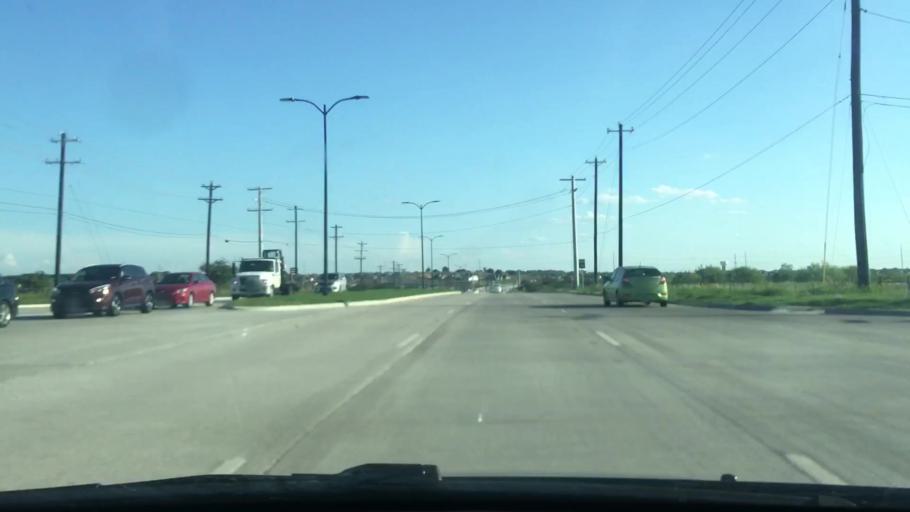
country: US
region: Texas
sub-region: Denton County
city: Little Elm
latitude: 33.2108
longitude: -96.8805
